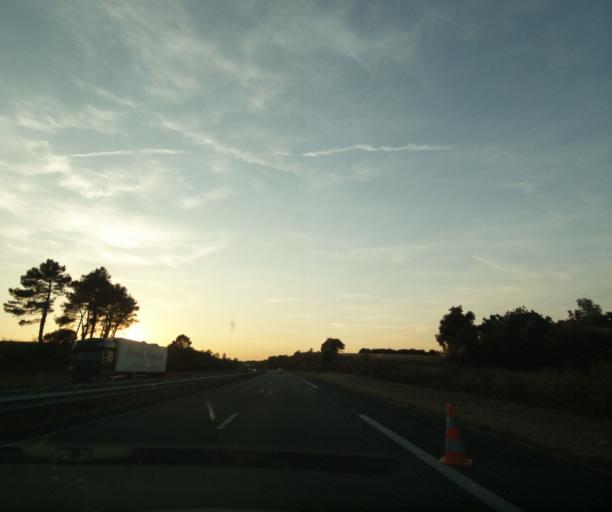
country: FR
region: Aquitaine
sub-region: Departement du Lot-et-Garonne
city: Meilhan-sur-Garonne
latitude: 44.4943
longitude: -0.0064
